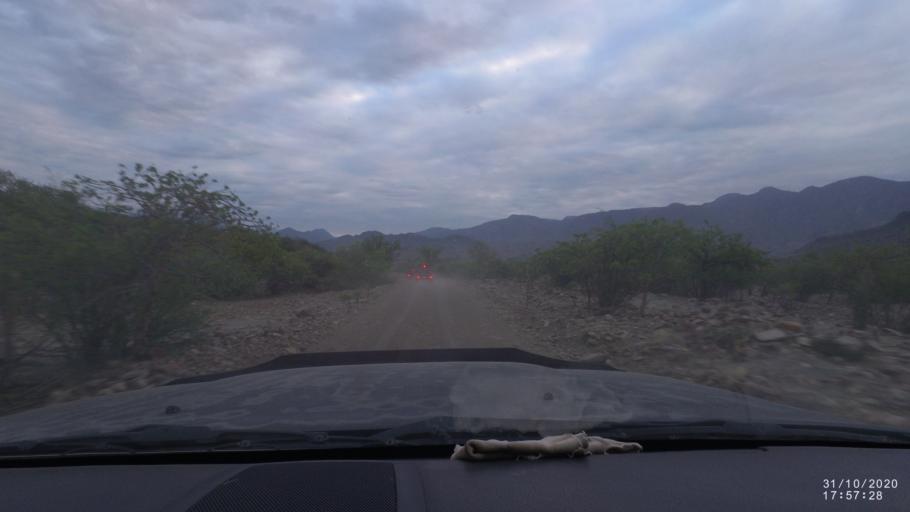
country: BO
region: Chuquisaca
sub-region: Provincia Zudanez
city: Mojocoya
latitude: -18.6507
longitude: -64.5320
